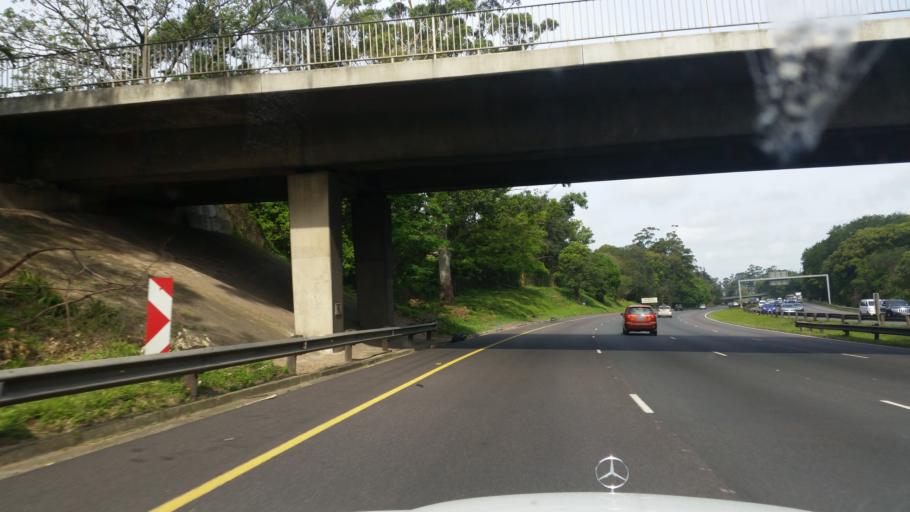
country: ZA
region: KwaZulu-Natal
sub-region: eThekwini Metropolitan Municipality
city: Berea
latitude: -29.8368
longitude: 30.9085
